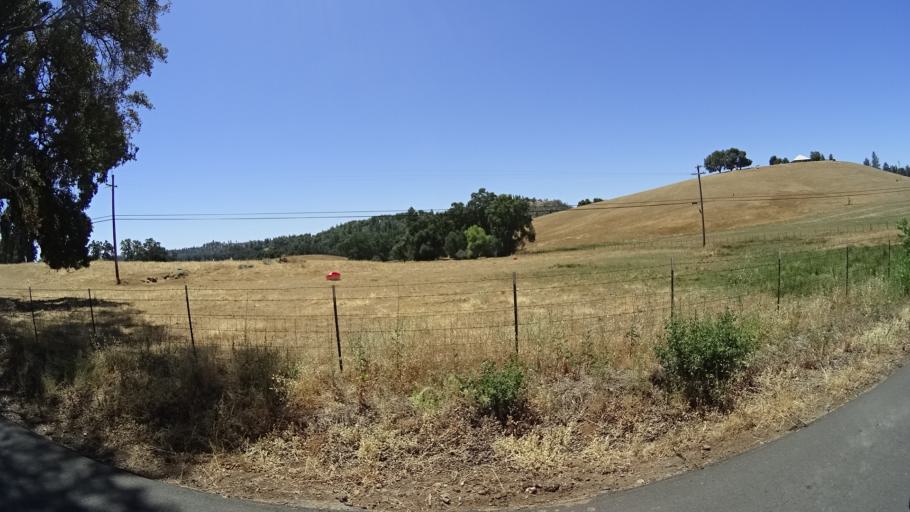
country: US
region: California
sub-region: Calaveras County
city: Mountain Ranch
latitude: 38.2317
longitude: -120.5490
